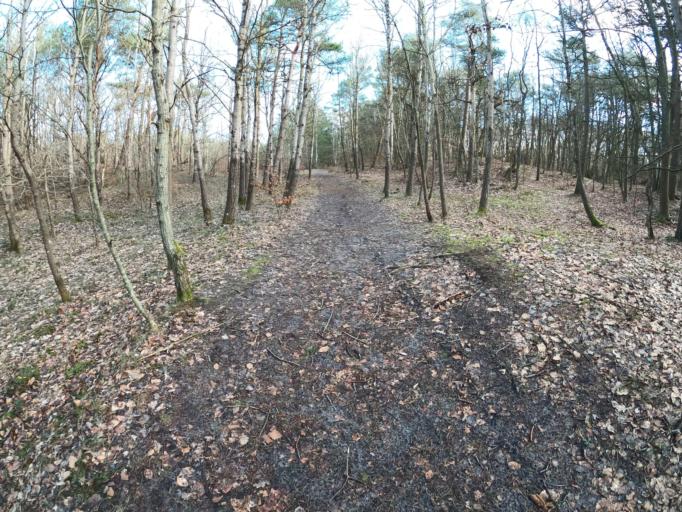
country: PL
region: West Pomeranian Voivodeship
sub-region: Powiat koszalinski
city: Sianow
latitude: 54.3182
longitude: 16.2128
